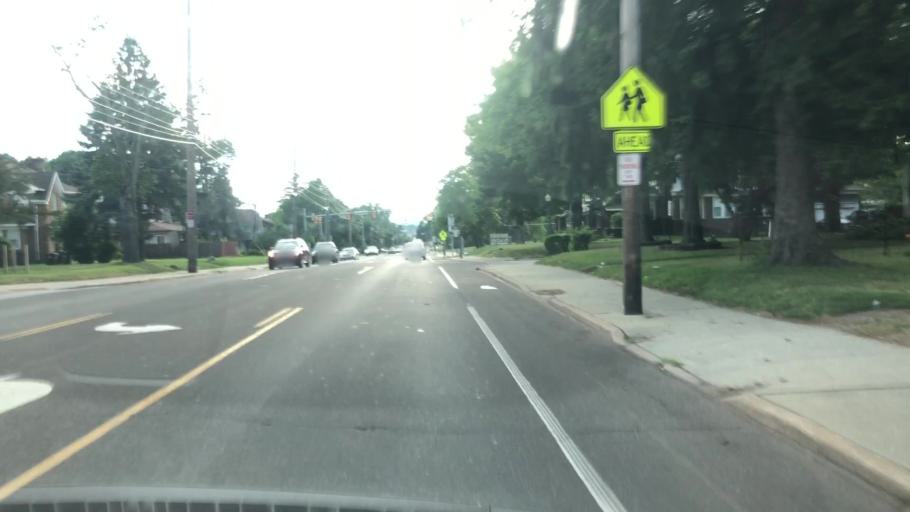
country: US
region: Ohio
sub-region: Summit County
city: Akron
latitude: 41.0839
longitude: -81.5578
